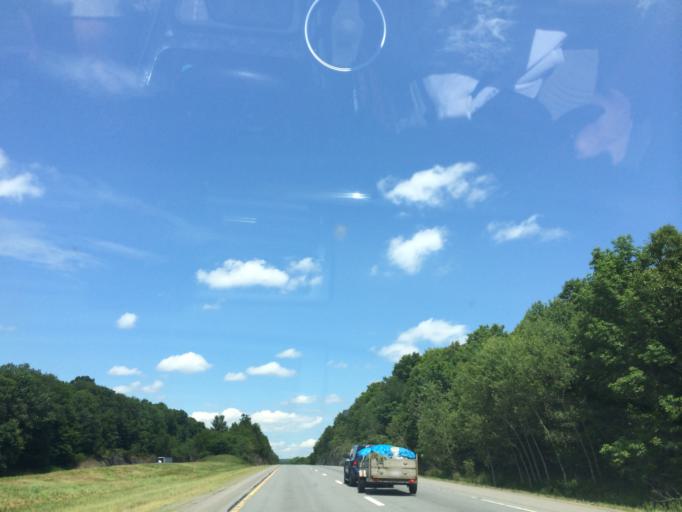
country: US
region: Pennsylvania
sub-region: Lackawanna County
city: Mount Cobb
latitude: 41.3792
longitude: -75.4545
